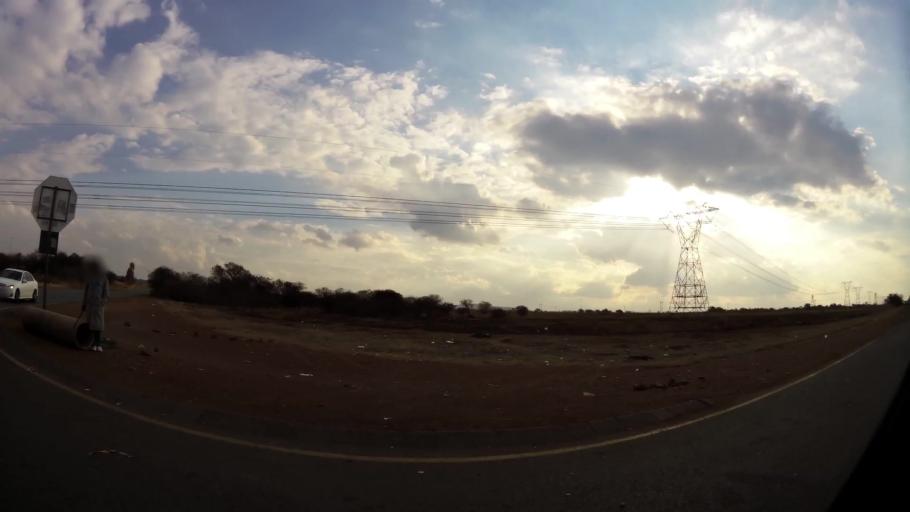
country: ZA
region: Gauteng
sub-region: Sedibeng District Municipality
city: Vereeniging
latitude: -26.6499
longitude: 27.8775
